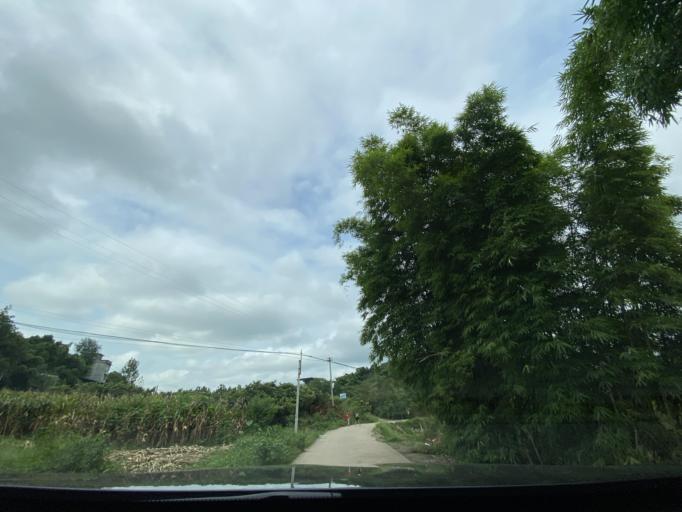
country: CN
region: Sichuan
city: Jiancheng
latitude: 30.4014
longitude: 104.5681
